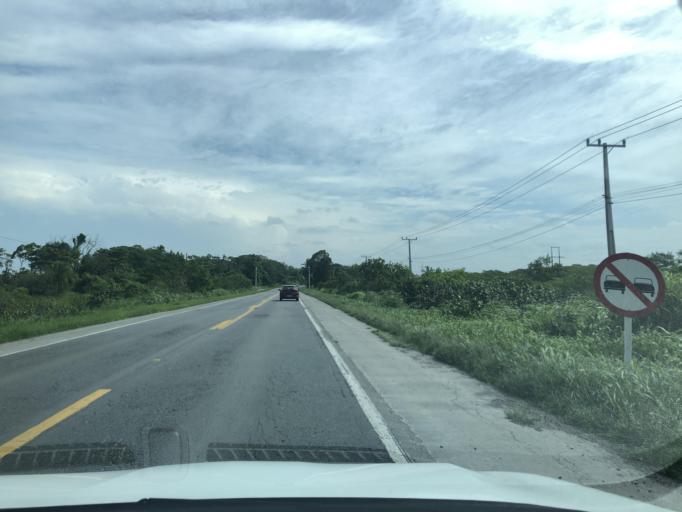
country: BR
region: Santa Catarina
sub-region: Sao Francisco Do Sul
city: Sao Francisco do Sul
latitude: -26.3526
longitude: -48.6593
